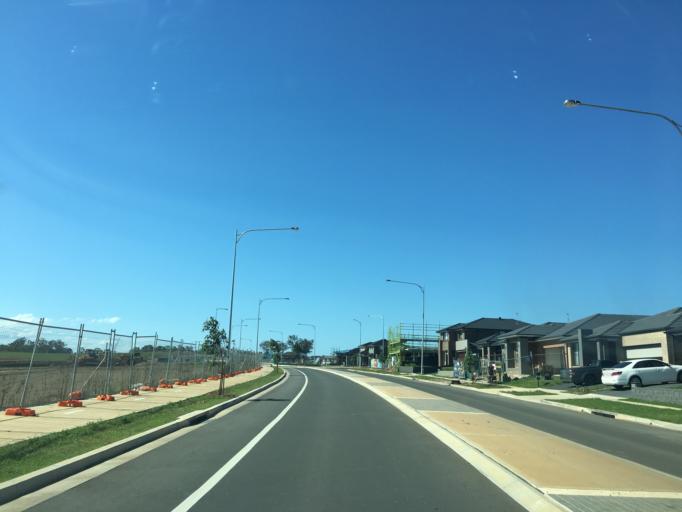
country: AU
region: New South Wales
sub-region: Campbelltown Municipality
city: Denham Court
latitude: -33.9945
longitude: 150.7945
